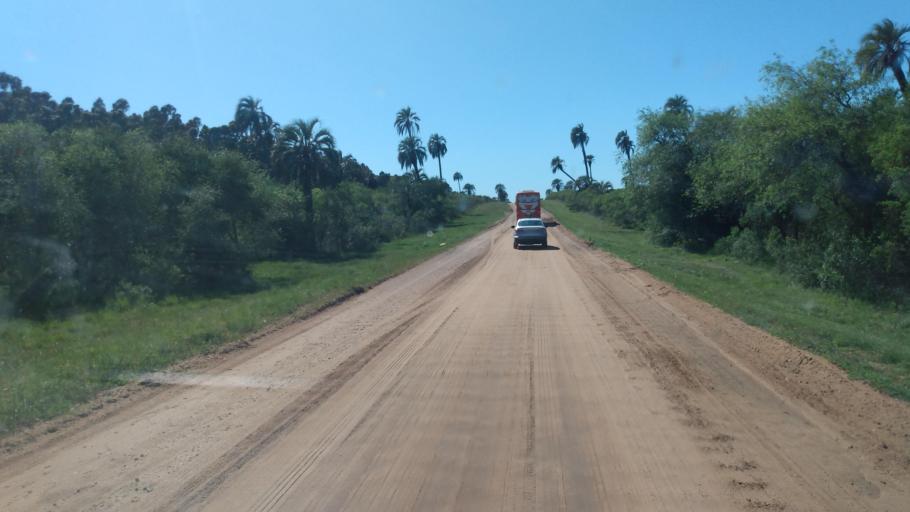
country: AR
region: Entre Rios
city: Ubajay
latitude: -31.8546
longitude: -58.2909
